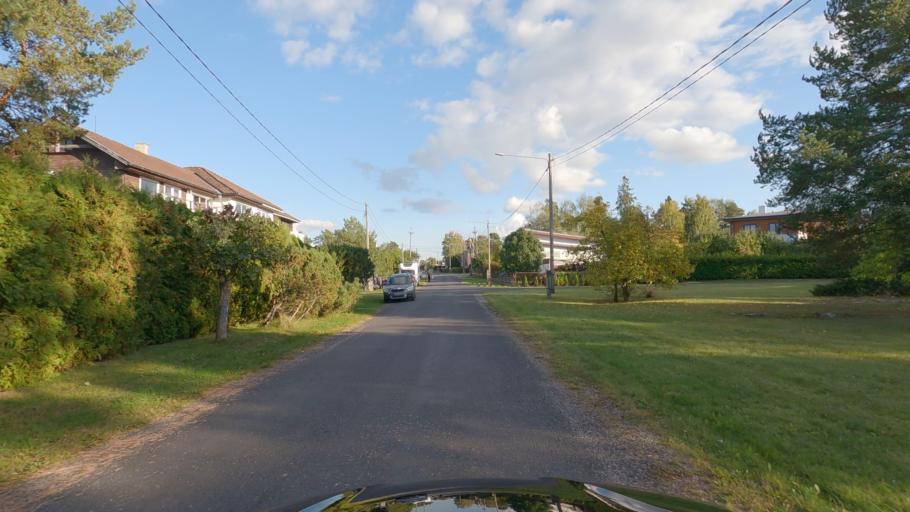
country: EE
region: Harju
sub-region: Saku vald
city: Saku
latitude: 59.3081
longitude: 24.6434
